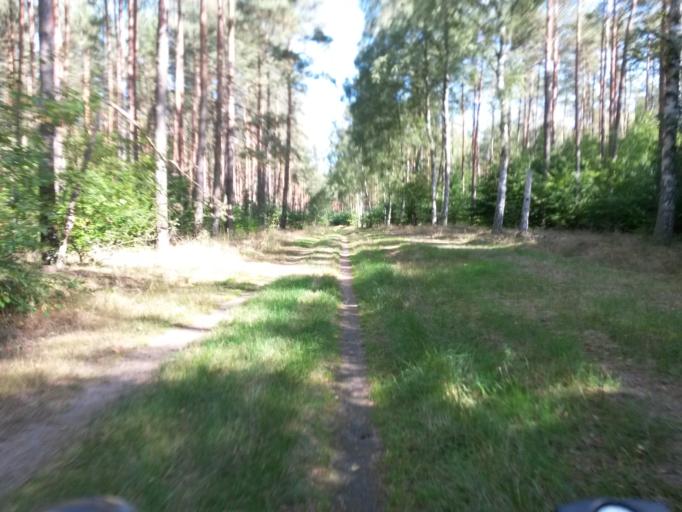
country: DE
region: Brandenburg
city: Lychen
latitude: 53.1516
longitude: 13.3732
